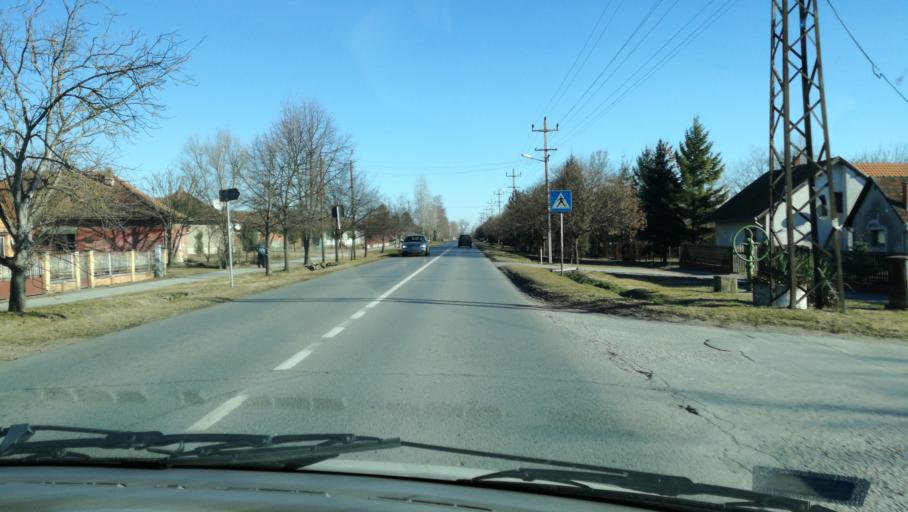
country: HU
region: Csongrad
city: Asotthalom
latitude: 46.1102
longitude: 19.8214
